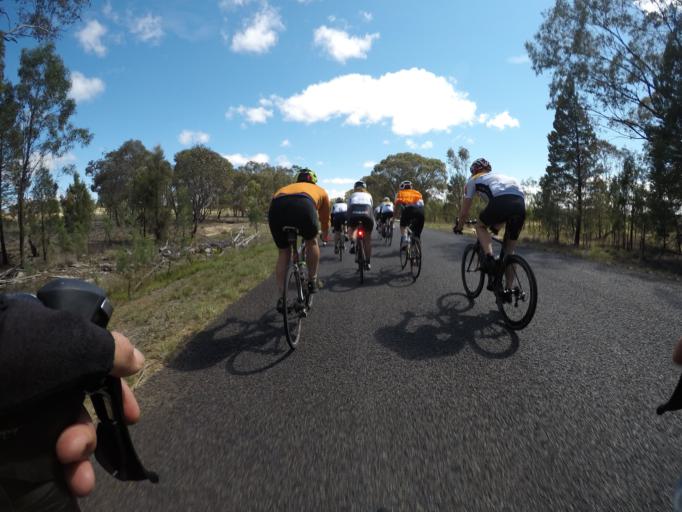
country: AU
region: New South Wales
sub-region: Dubbo Municipality
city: Eulomogo
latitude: -32.6143
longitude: 148.5490
